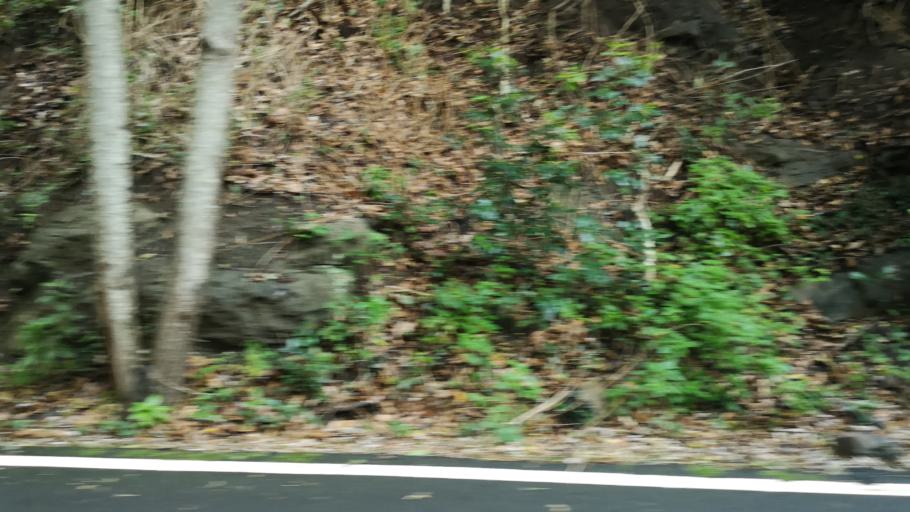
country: ES
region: Canary Islands
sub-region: Provincia de Santa Cruz de Tenerife
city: Hermigua
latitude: 28.1277
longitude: -17.2068
